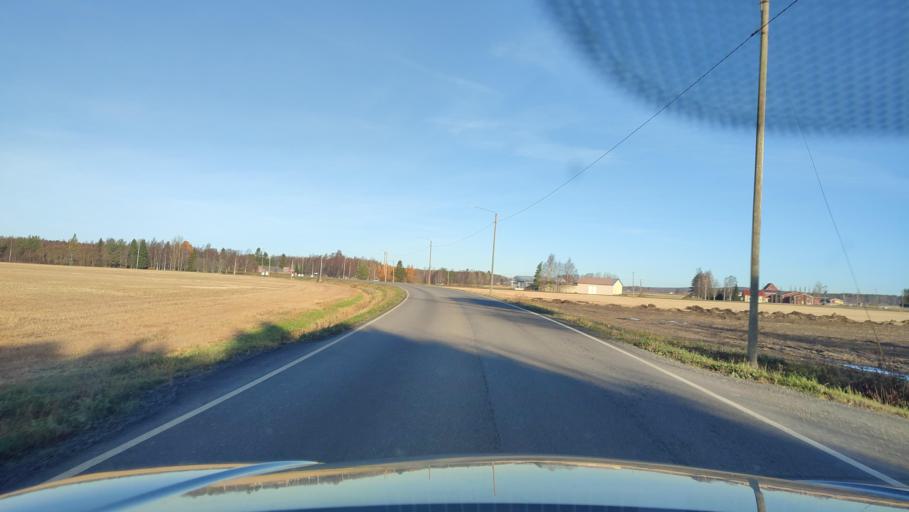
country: FI
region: Southern Ostrobothnia
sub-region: Suupohja
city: Karijoki
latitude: 62.2973
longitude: 21.7203
